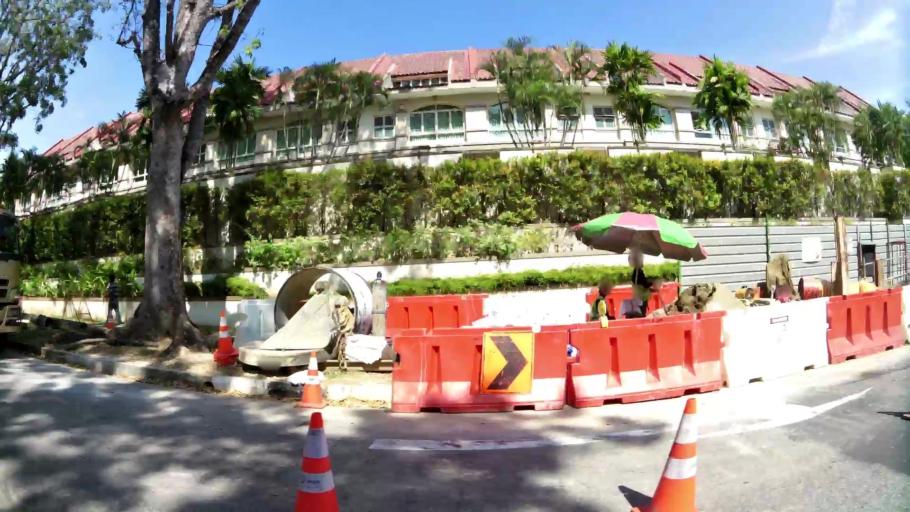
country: SG
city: Singapore
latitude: 1.3777
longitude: 103.8359
